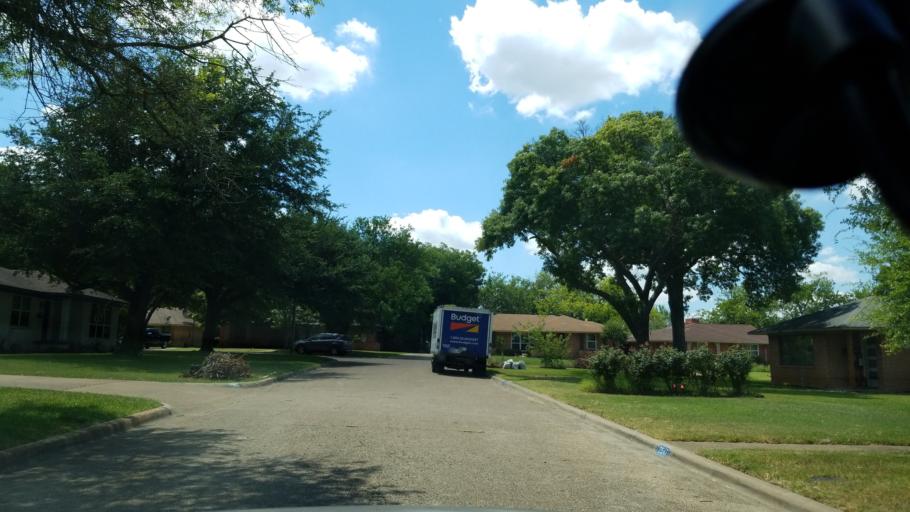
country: US
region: Texas
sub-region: Dallas County
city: Cockrell Hill
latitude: 32.7038
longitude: -96.8616
